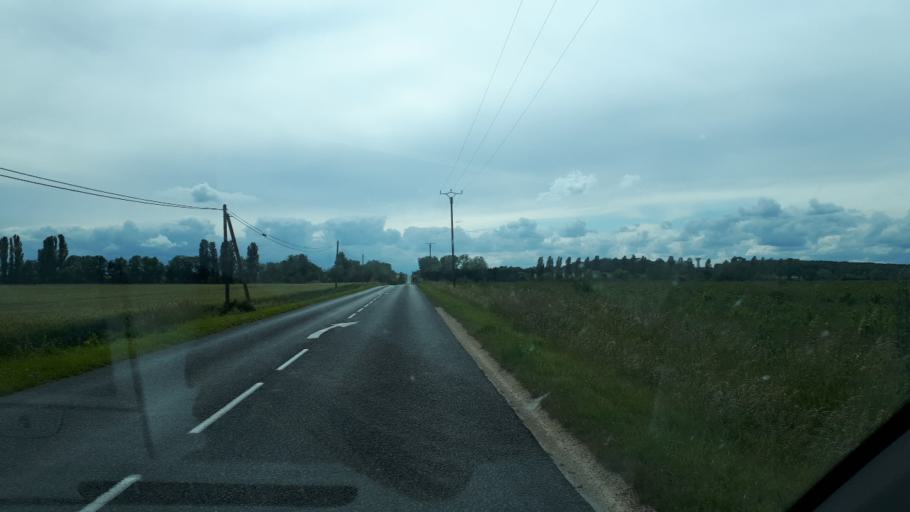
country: FR
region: Centre
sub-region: Departement du Cher
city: La Chapelle-Saint-Ursin
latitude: 47.0809
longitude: 2.3263
